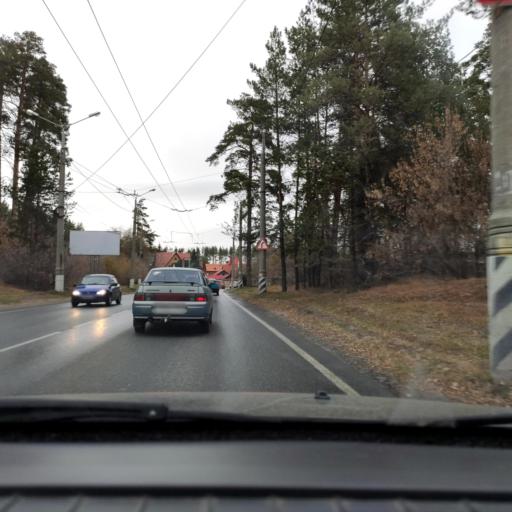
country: RU
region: Samara
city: Tol'yatti
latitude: 53.4779
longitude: 49.3499
